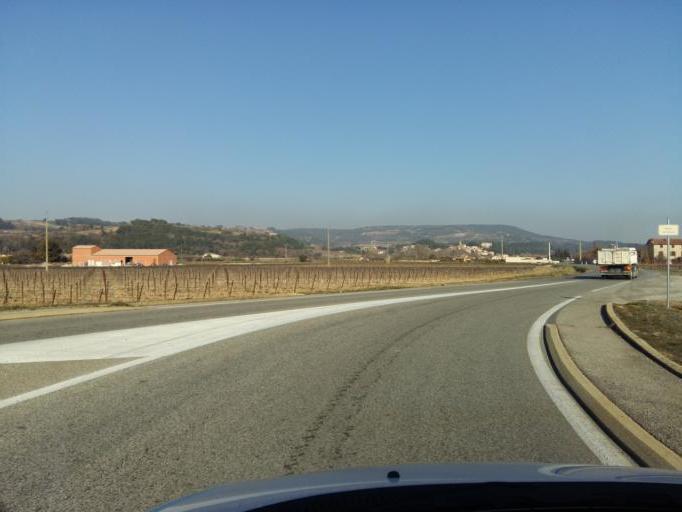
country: FR
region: Provence-Alpes-Cote d'Azur
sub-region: Departement du Vaucluse
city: Sablet
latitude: 44.2339
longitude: 5.0169
